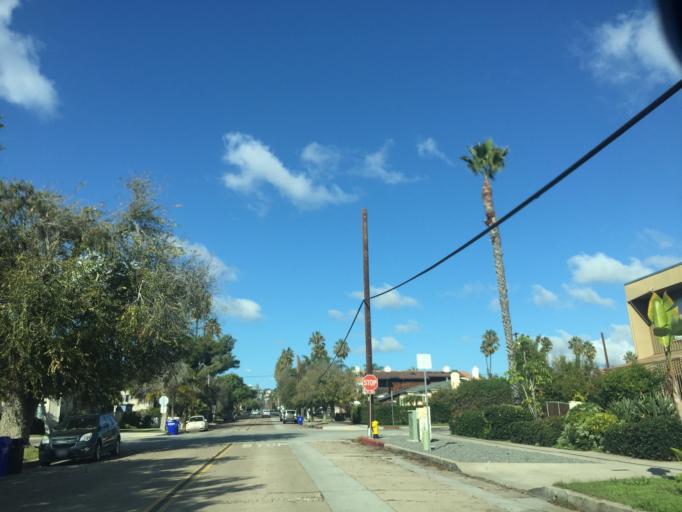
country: US
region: California
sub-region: San Diego County
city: La Jolla
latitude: 32.7953
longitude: -117.2453
